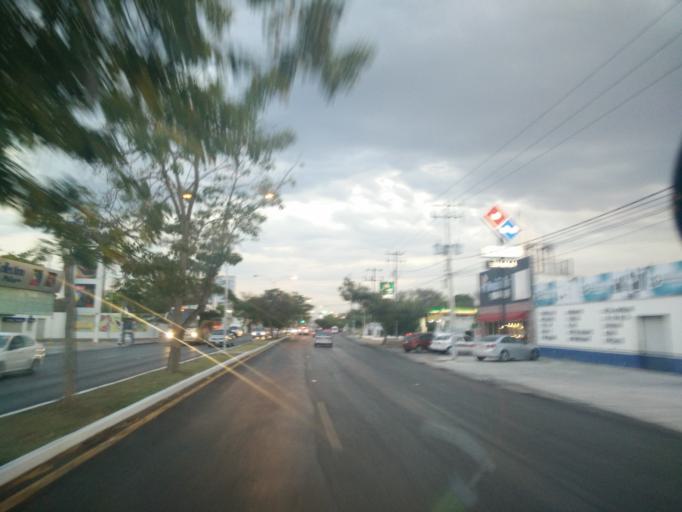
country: MX
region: Yucatan
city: Merida
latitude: 20.9591
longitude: -89.6422
